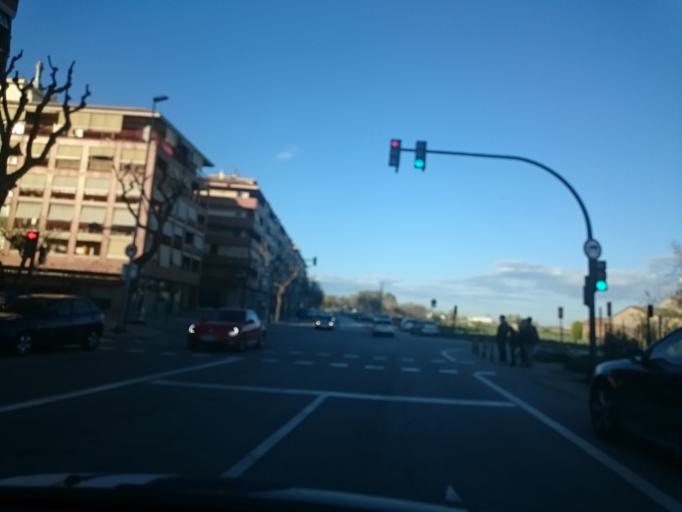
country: ES
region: Catalonia
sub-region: Provincia de Barcelona
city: El Prat de Llobregat
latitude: 41.3220
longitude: 2.1036
